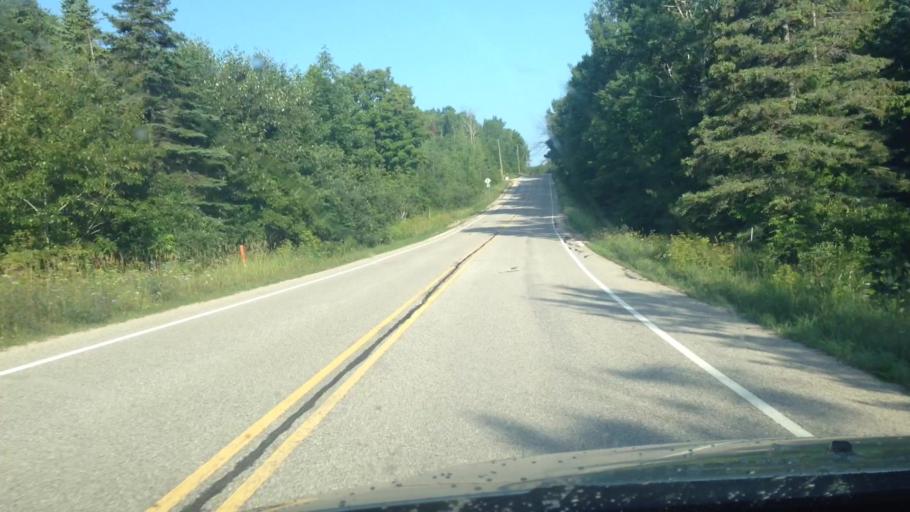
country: US
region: Michigan
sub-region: Mackinac County
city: Saint Ignace
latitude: 45.8914
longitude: -84.7913
